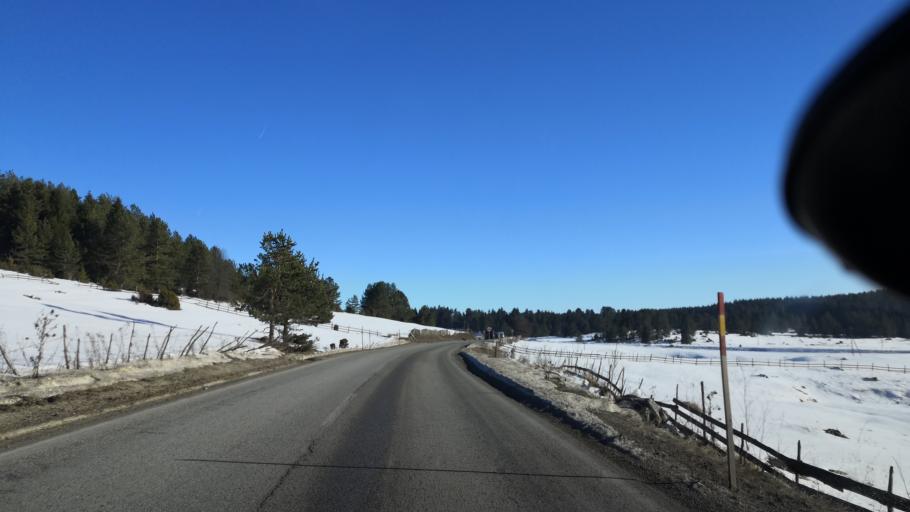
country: BA
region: Republika Srpska
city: Sokolac
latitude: 43.9212
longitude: 18.6839
